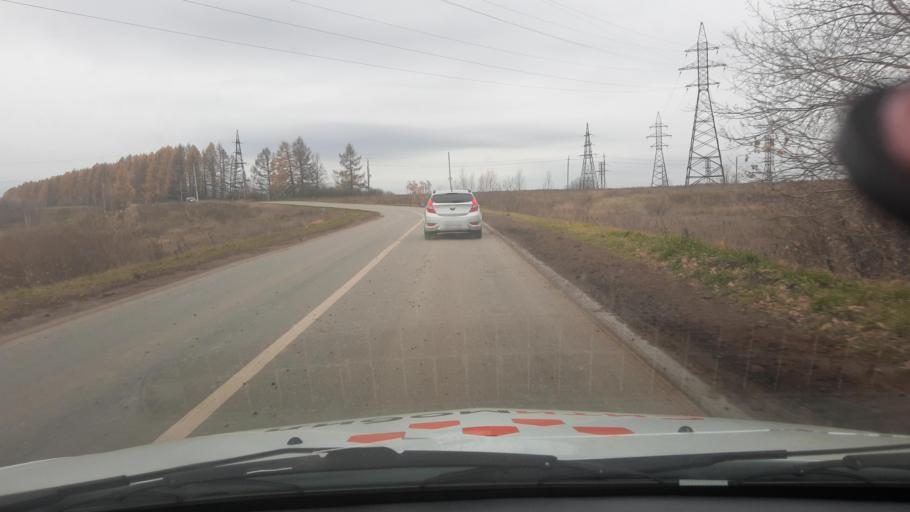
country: RU
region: Bashkortostan
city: Iglino
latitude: 54.7523
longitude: 56.2501
